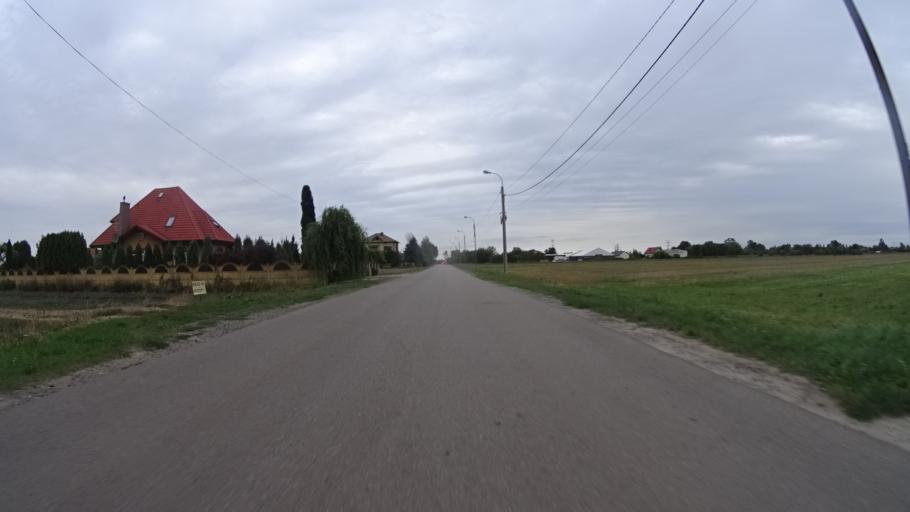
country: PL
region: Masovian Voivodeship
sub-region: Powiat warszawski zachodni
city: Hornowek
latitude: 52.2514
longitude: 20.7898
